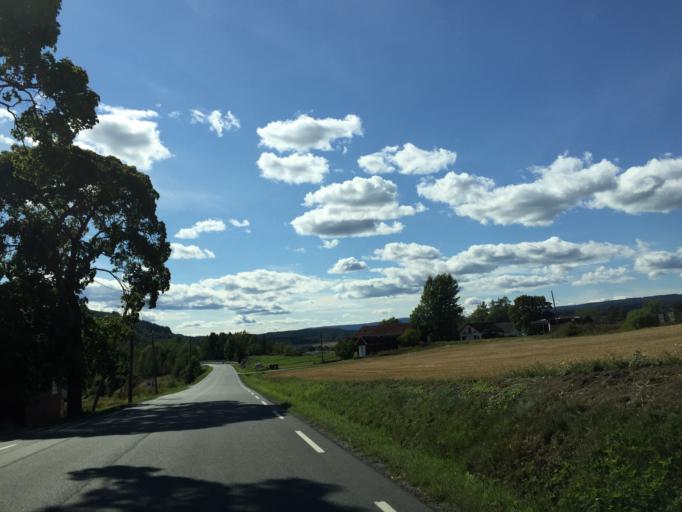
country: NO
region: Buskerud
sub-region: Ovre Eiker
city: Hokksund
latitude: 59.7017
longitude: 9.8490
